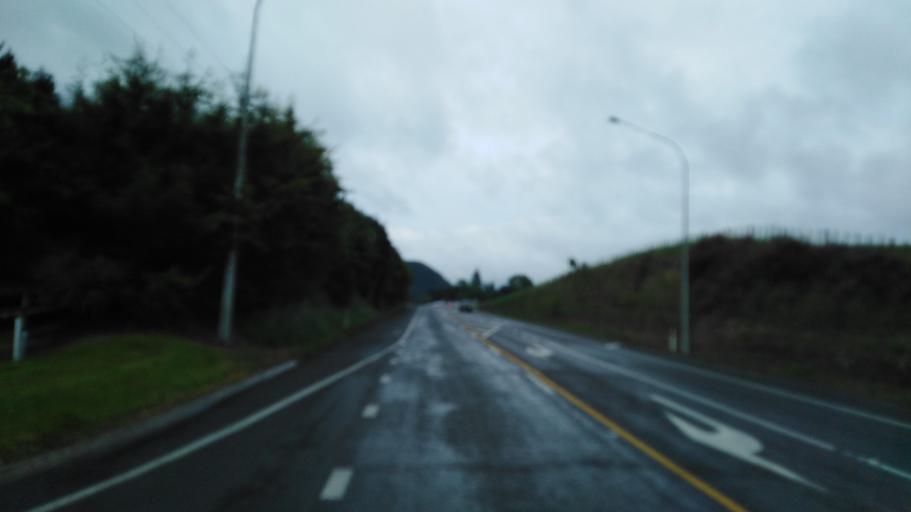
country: NZ
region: Wellington
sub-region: Kapiti Coast District
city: Otaki
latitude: -40.7284
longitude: 175.2071
